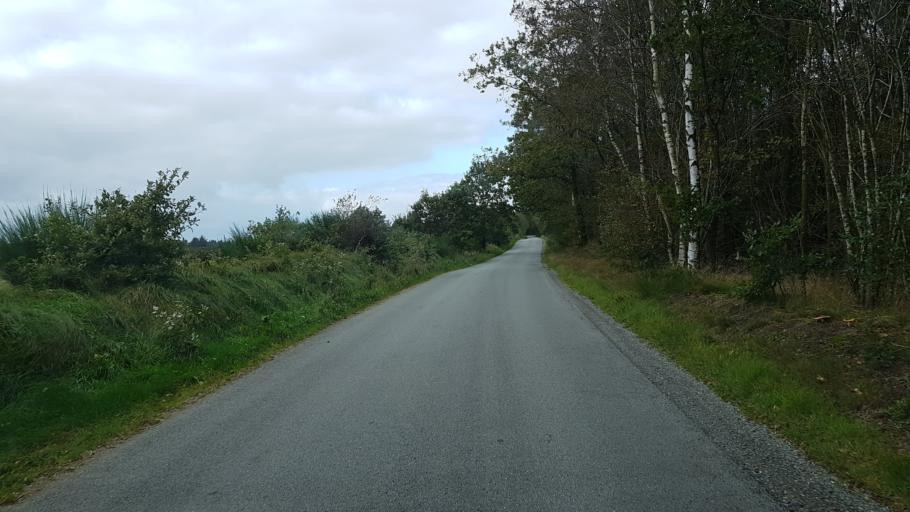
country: DK
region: South Denmark
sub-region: Billund Kommune
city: Grindsted
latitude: 55.6930
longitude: 8.7753
